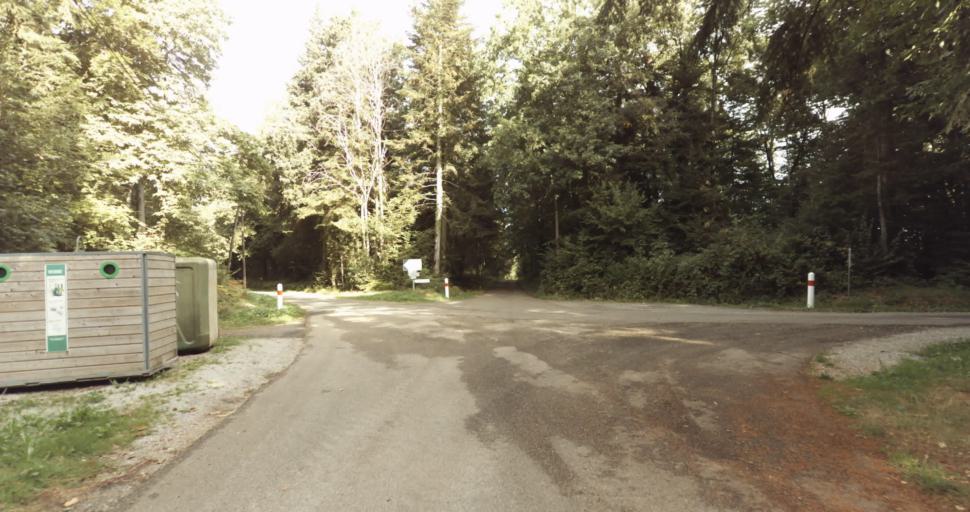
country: FR
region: Lower Normandy
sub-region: Departement de l'Orne
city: Gace
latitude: 48.8247
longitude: 0.2324
